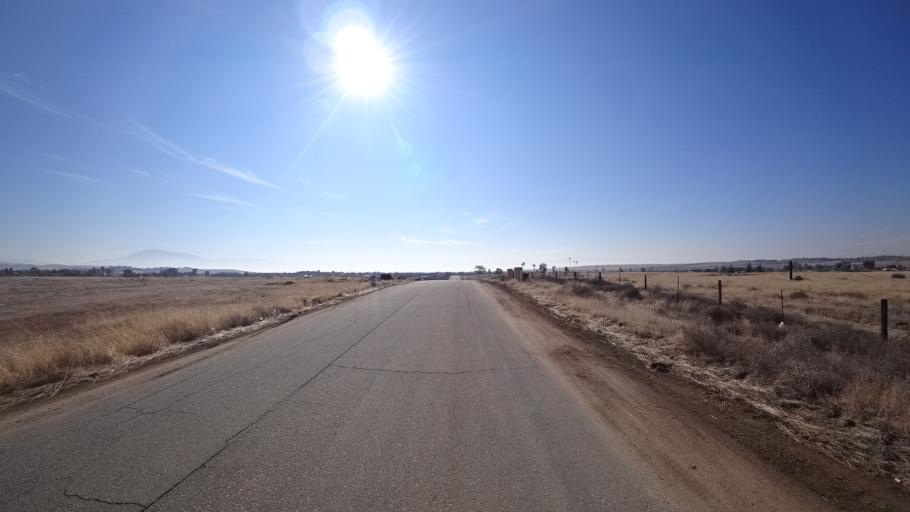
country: US
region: California
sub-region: Kern County
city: Oildale
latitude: 35.4191
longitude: -118.8924
